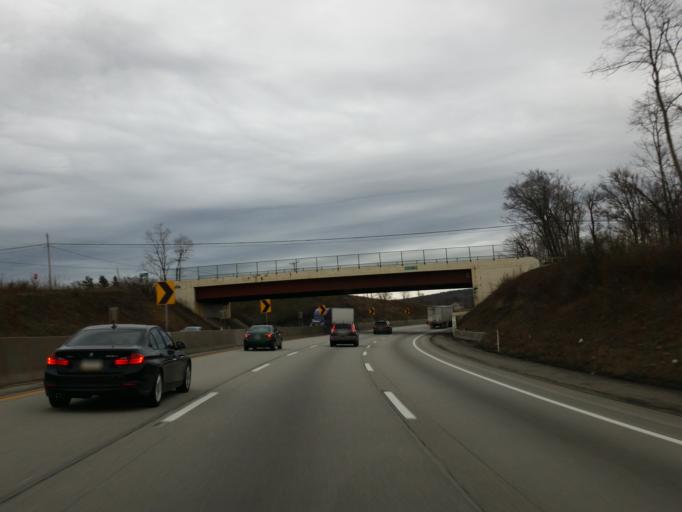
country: US
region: Pennsylvania
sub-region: Westmoreland County
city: Ligonier
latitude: 40.1290
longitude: -79.2916
